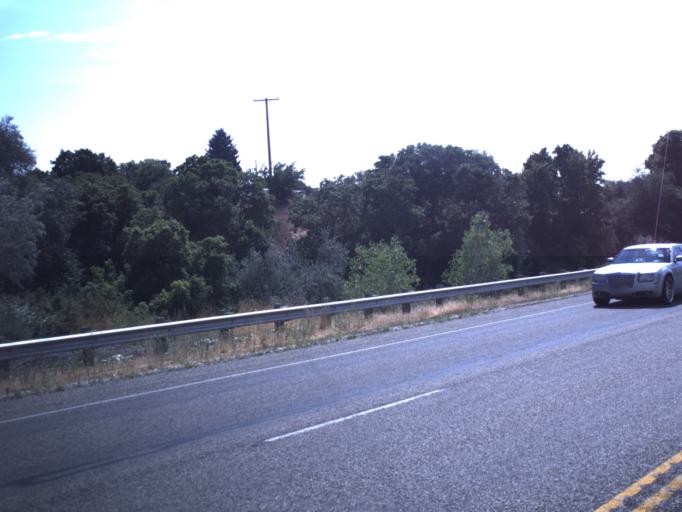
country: US
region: Utah
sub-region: Box Elder County
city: Garland
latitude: 41.7886
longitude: -112.0784
